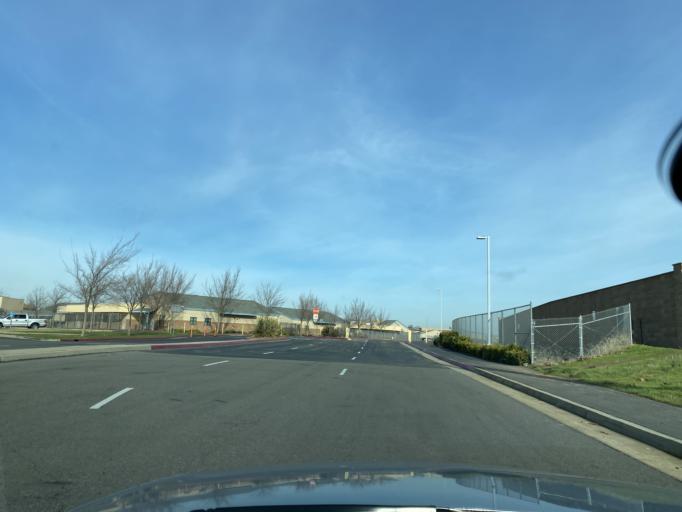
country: US
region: California
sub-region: Sacramento County
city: Elk Grove
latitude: 38.3947
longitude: -121.3956
